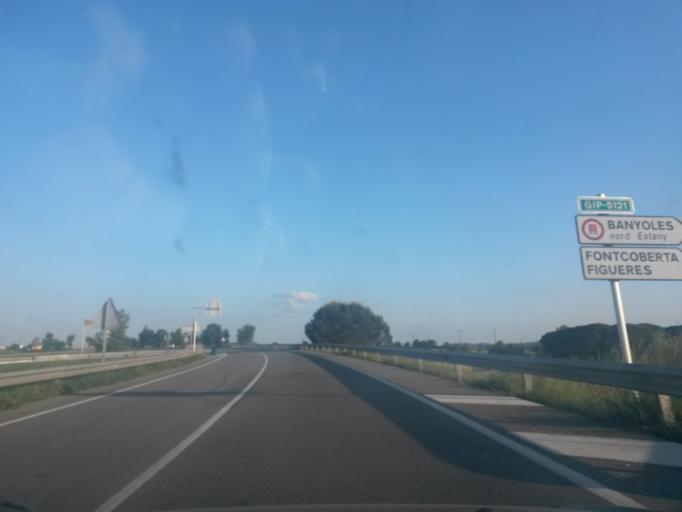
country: ES
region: Catalonia
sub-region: Provincia de Girona
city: Banyoles
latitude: 42.1414
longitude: 2.7635
